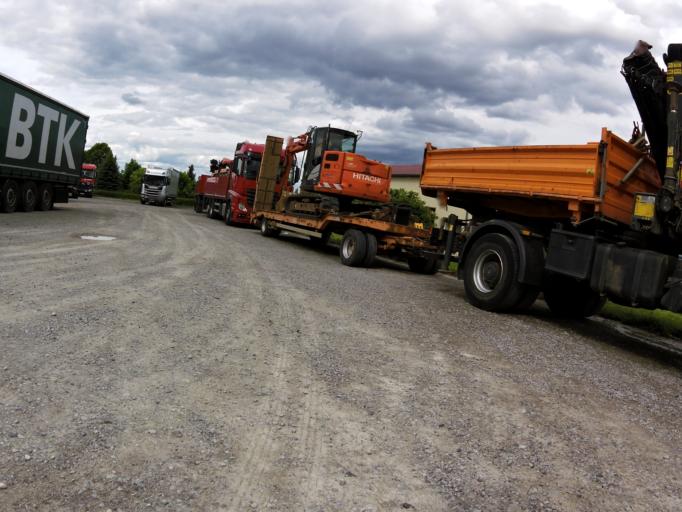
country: DE
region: Thuringia
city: Langula
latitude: 51.1486
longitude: 10.4221
